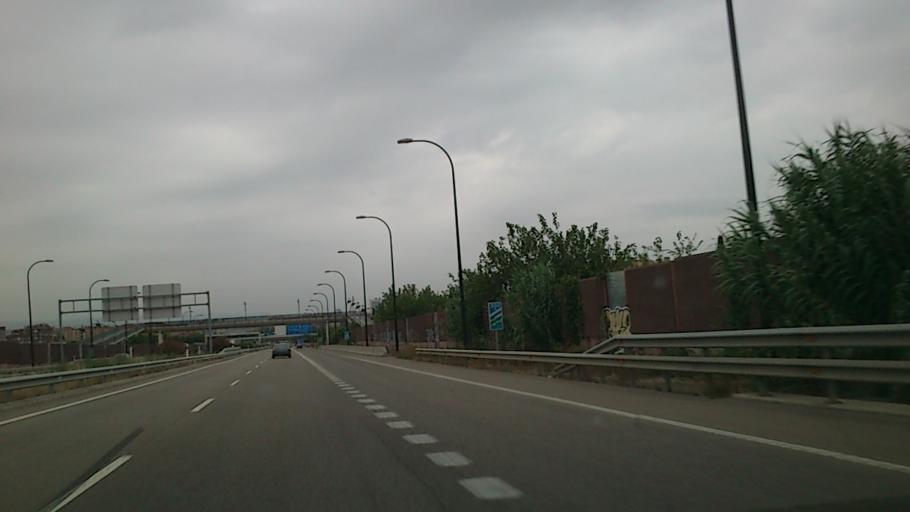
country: ES
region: Aragon
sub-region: Provincia de Zaragoza
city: Zaragoza
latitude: 41.6858
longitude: -0.8735
